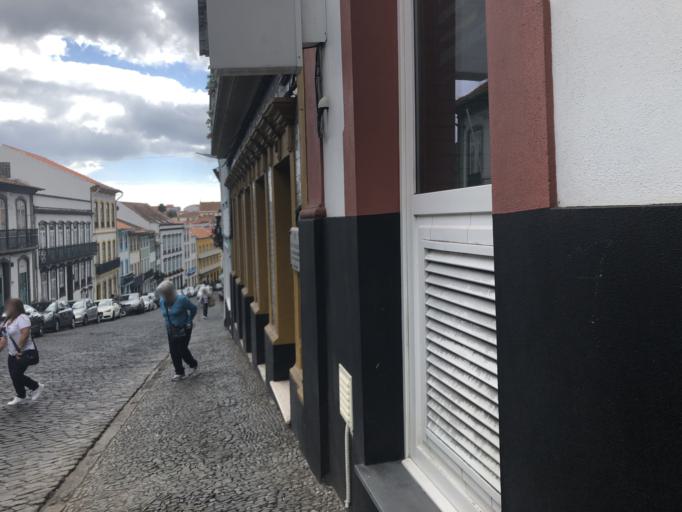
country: PT
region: Azores
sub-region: Angra do Heroismo
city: Angra do Heroismo
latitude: 38.6559
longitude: -27.2164
